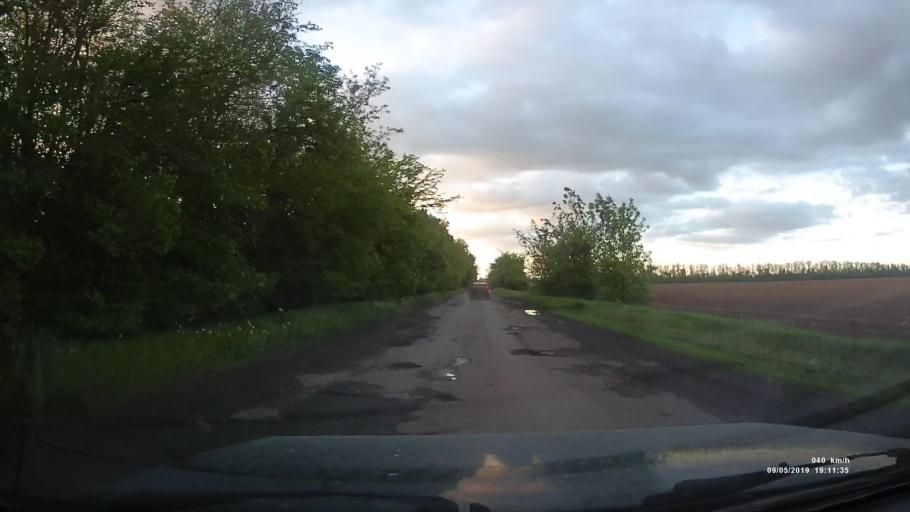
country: RU
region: Krasnodarskiy
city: Kanelovskaya
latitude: 46.7362
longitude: 39.2136
